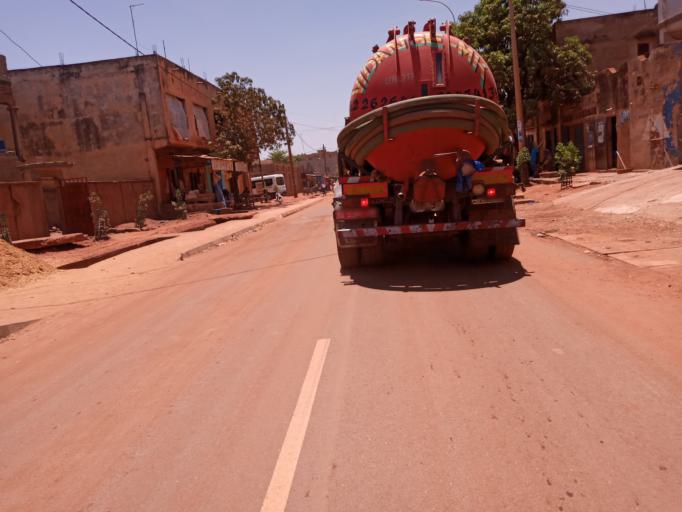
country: ML
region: Bamako
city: Bamako
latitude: 12.5910
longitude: -7.9827
